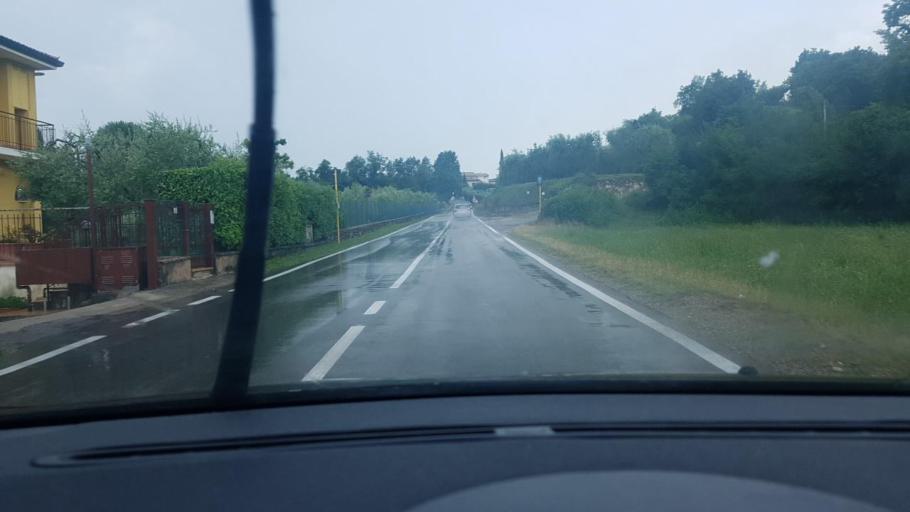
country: IT
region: Veneto
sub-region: Provincia di Verona
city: Garda
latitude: 45.5965
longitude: 10.7162
